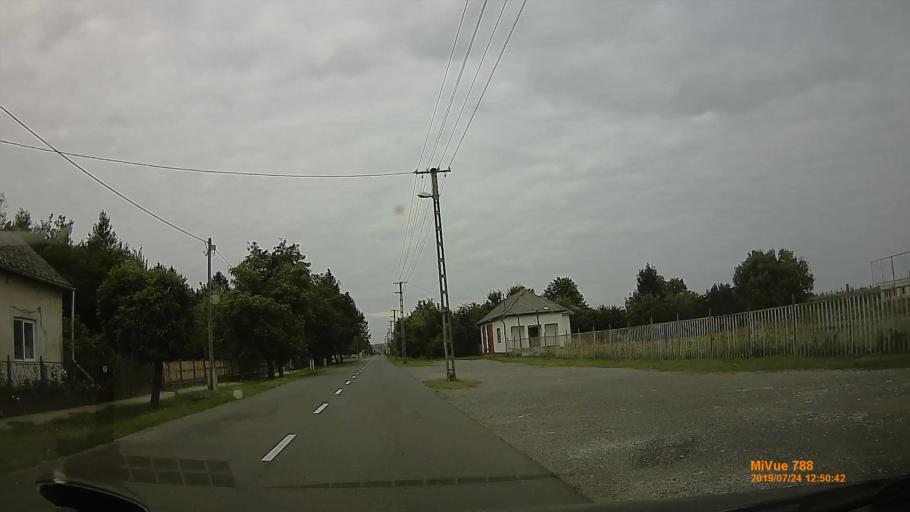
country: HU
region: Szabolcs-Szatmar-Bereg
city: Aranyosapati
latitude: 48.1894
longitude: 22.3083
